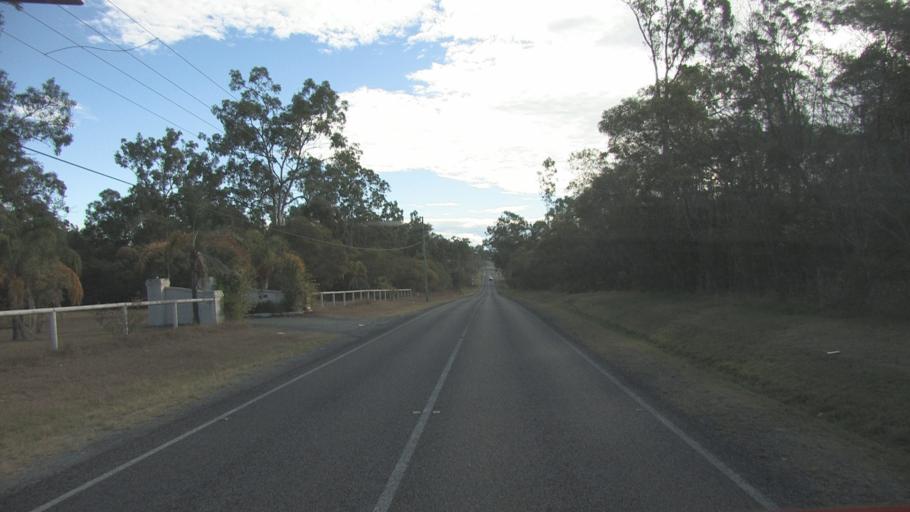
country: AU
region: Queensland
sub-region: Logan
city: Cedar Vale
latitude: -27.8353
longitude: 153.0419
